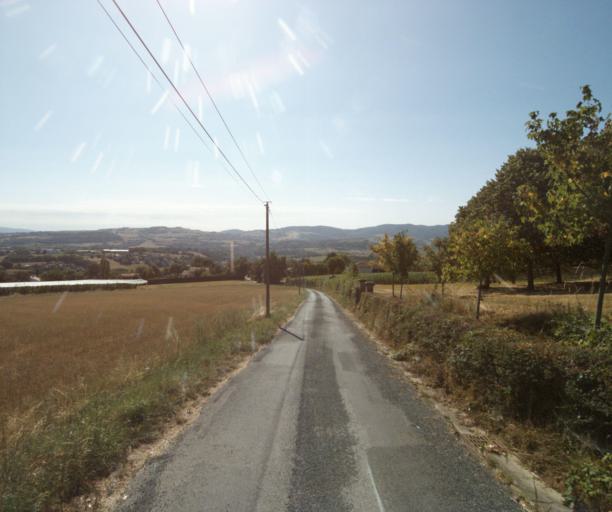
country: FR
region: Rhone-Alpes
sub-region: Departement du Rhone
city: Savigny
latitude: 45.8213
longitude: 4.5669
